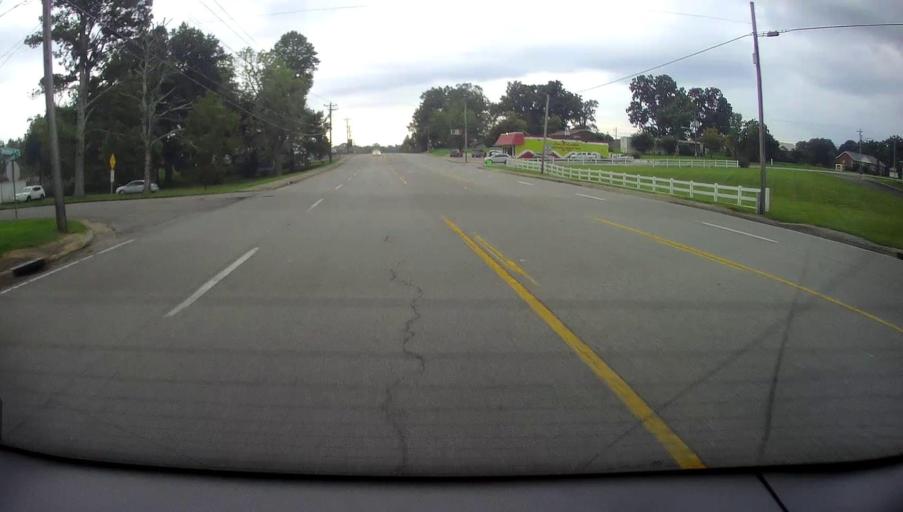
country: US
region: Tennessee
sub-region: Coffee County
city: Manchester
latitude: 35.4947
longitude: -86.0876
